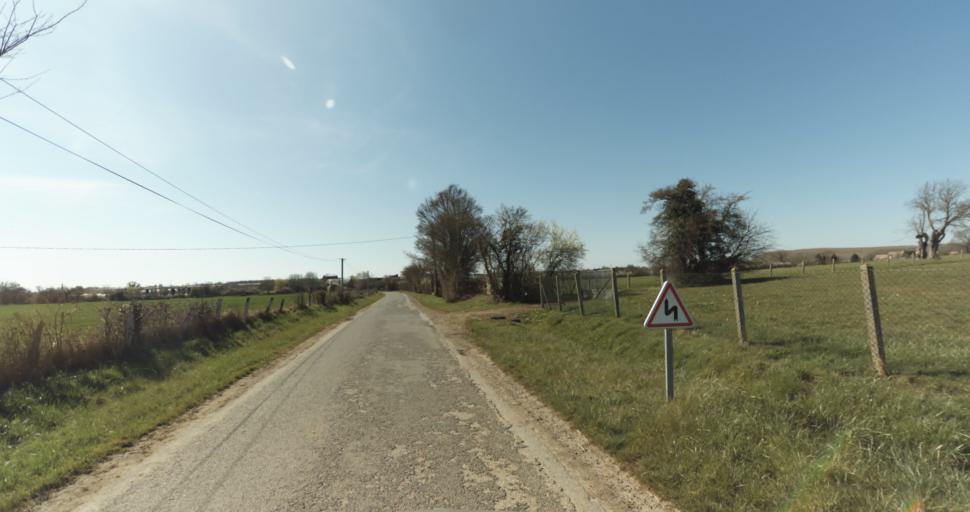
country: FR
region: Lower Normandy
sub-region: Departement du Calvados
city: Saint-Pierre-sur-Dives
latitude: 49.0513
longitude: -0.0289
